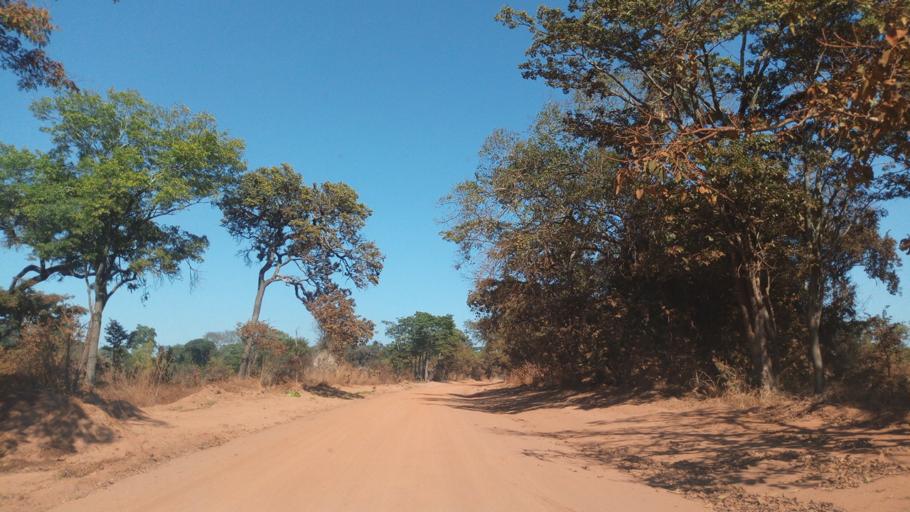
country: ZM
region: Luapula
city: Mwense
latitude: -10.7374
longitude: 28.3378
